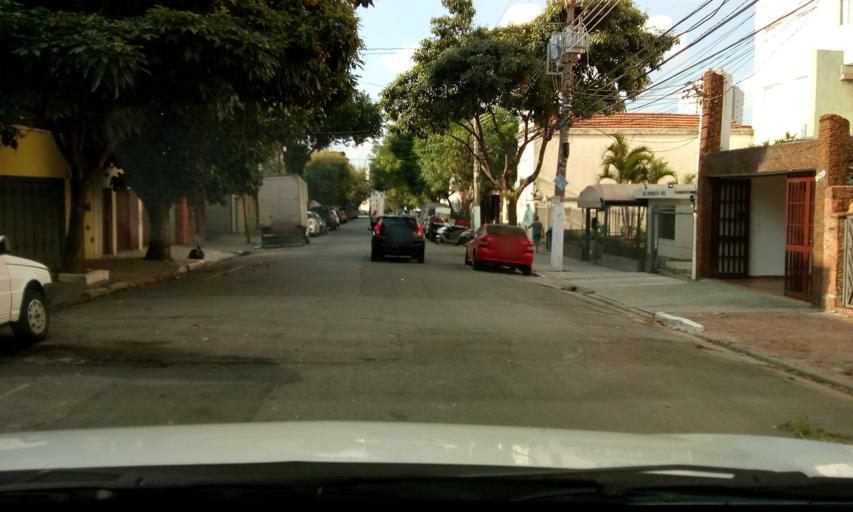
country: BR
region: Sao Paulo
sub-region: Sao Paulo
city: Sao Paulo
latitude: -23.5665
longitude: -46.6268
